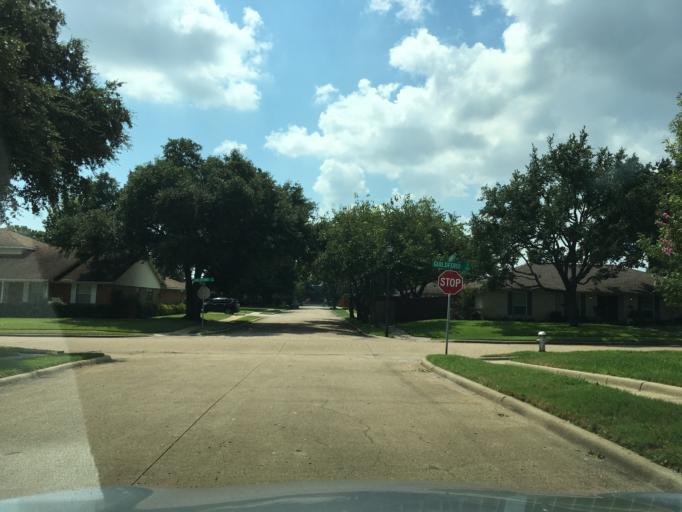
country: US
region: Texas
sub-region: Dallas County
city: Garland
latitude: 32.9376
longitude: -96.6467
